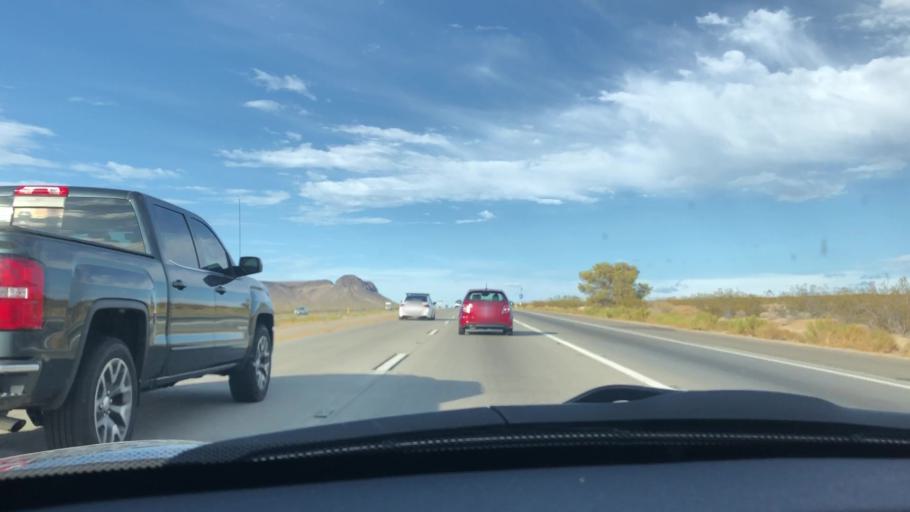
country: US
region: Nevada
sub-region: Clark County
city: Sandy Valley
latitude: 35.3807
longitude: -115.8697
